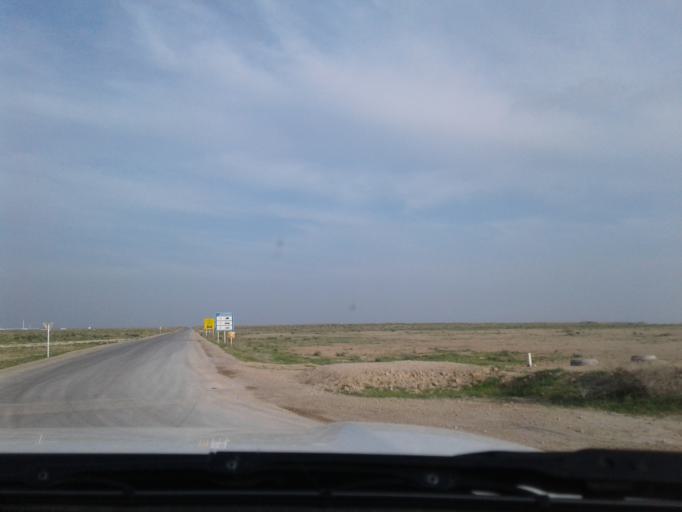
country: TM
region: Lebap
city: Sayat
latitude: 38.6351
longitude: 64.5819
